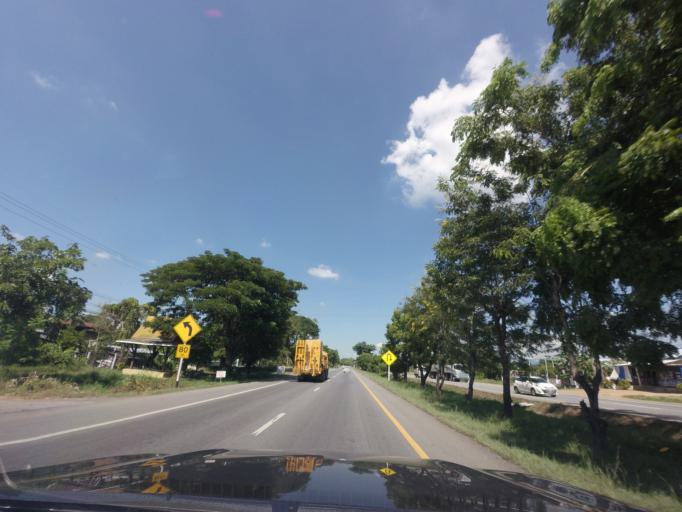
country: TH
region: Nakhon Ratchasima
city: Non Sung
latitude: 15.1442
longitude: 102.3205
